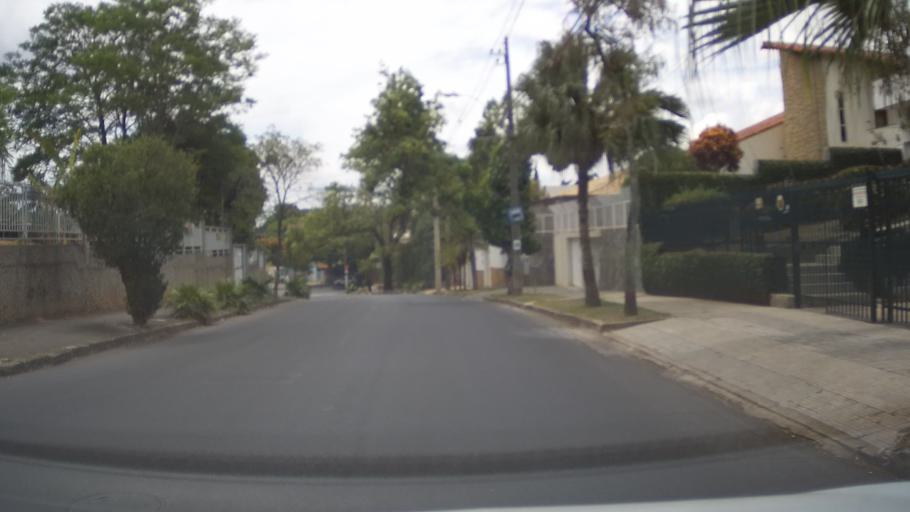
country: BR
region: Minas Gerais
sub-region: Belo Horizonte
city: Belo Horizonte
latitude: -19.8538
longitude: -43.9627
